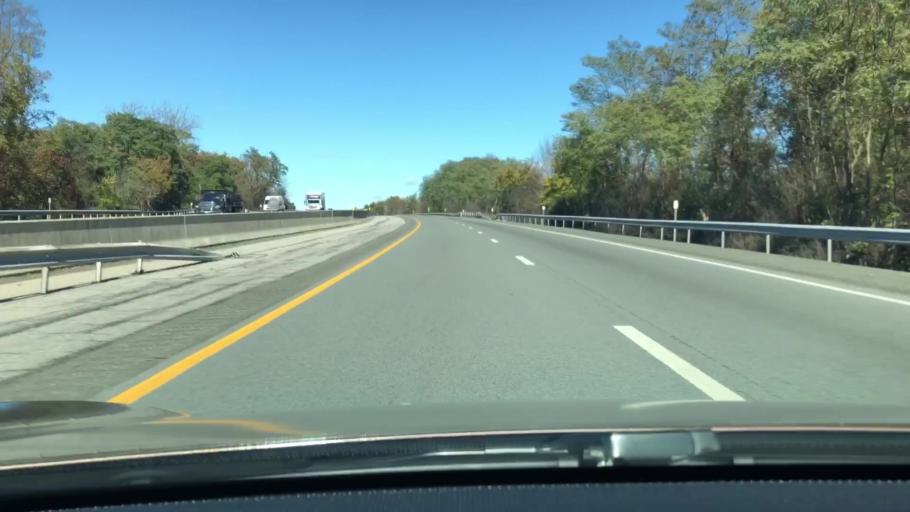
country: US
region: New York
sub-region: Orange County
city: Vails Gate
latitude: 41.4513
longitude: -74.0645
